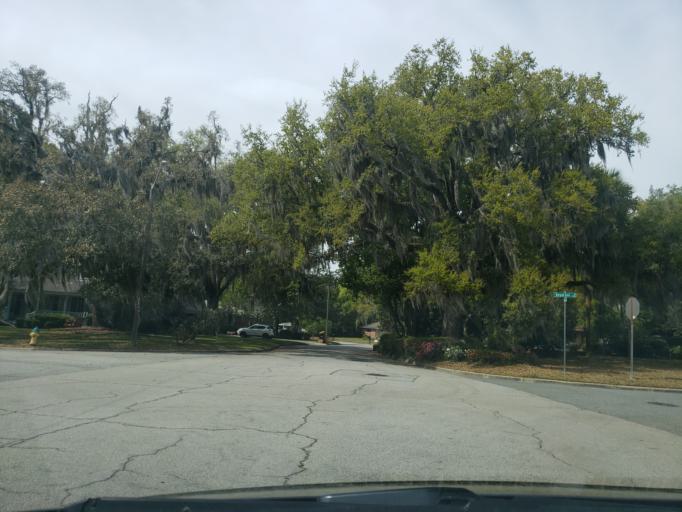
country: US
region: Georgia
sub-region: Chatham County
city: Isle of Hope
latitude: 31.9940
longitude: -81.0958
